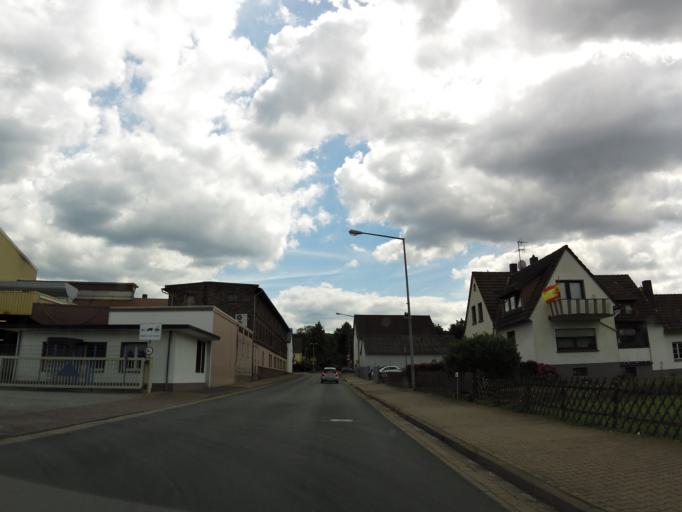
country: DE
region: Lower Saxony
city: Boffzen
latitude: 51.7507
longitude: 9.3969
